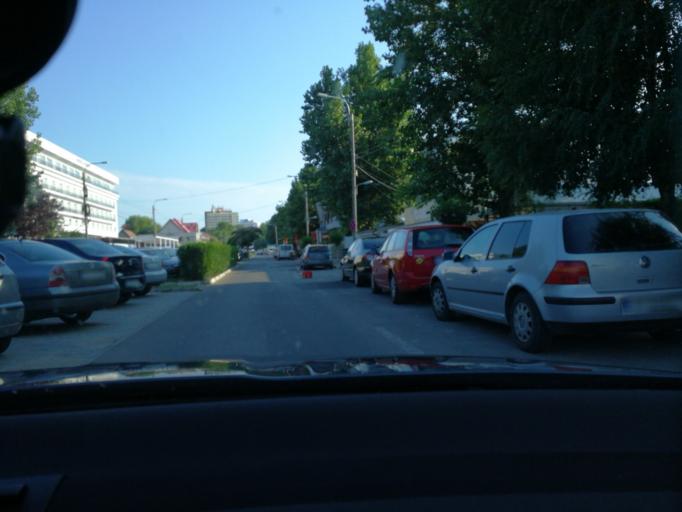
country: RO
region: Constanta
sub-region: Oras Eforie
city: Eforie Nord
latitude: 44.0695
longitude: 28.6380
